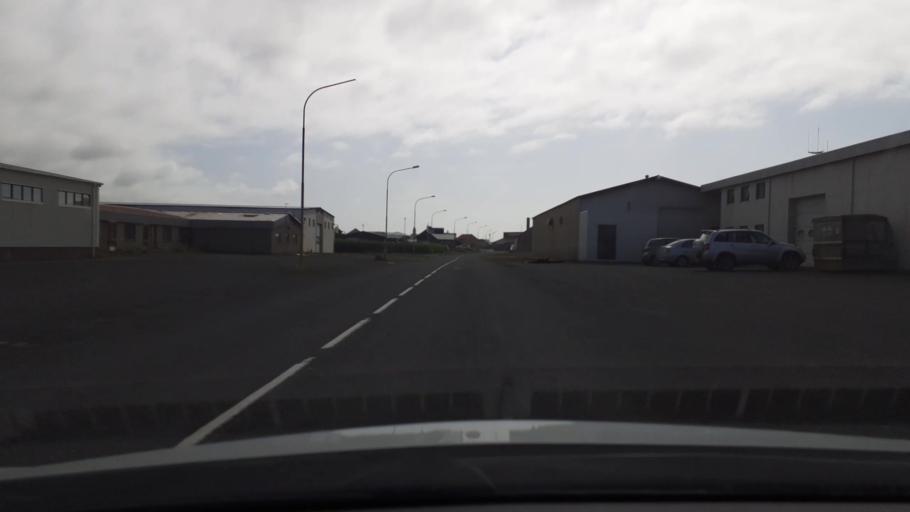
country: IS
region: South
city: Hveragerdi
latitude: 63.8668
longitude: -21.1625
